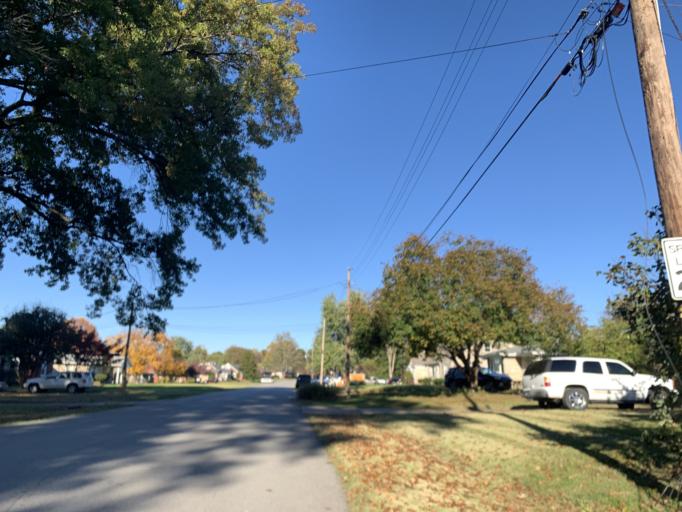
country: US
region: Kentucky
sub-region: Jefferson County
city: Saint Dennis
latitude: 38.1697
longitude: -85.8299
